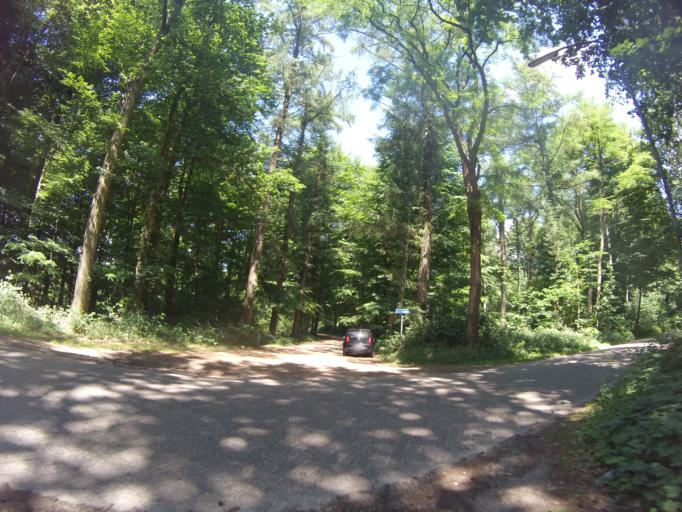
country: NL
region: Drenthe
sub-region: Gemeente Emmen
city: Emmen
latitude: 52.8014
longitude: 6.9115
